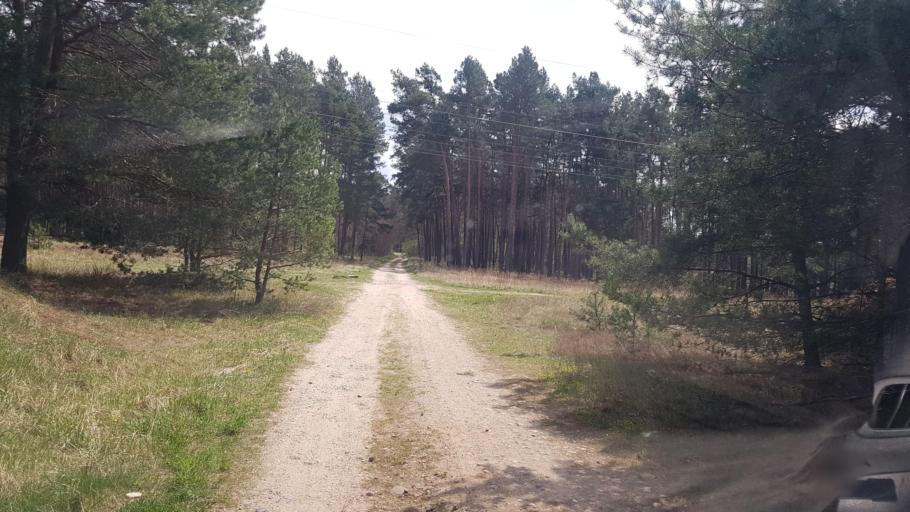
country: DE
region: Brandenburg
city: Luckenwalde
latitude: 52.1358
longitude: 13.1611
